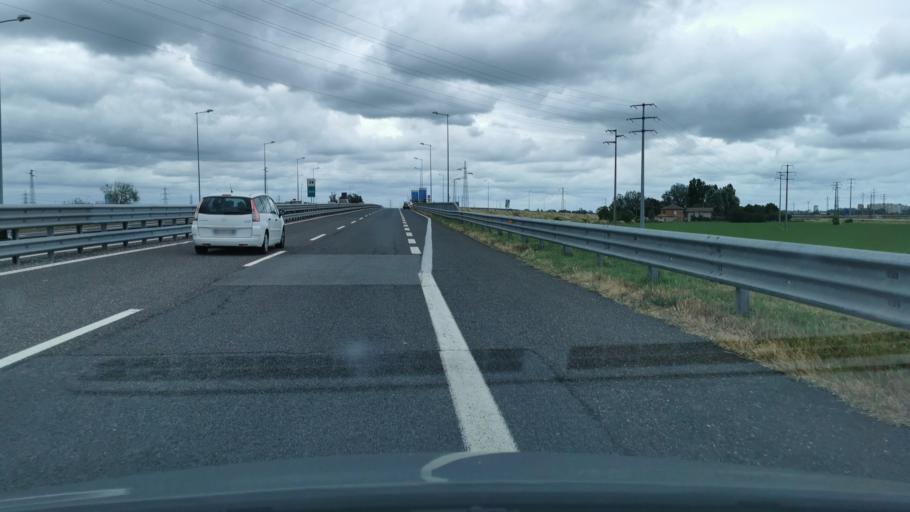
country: IT
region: Emilia-Romagna
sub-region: Provincia di Ravenna
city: Fornace Zarattini
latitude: 44.4258
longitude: 12.1511
